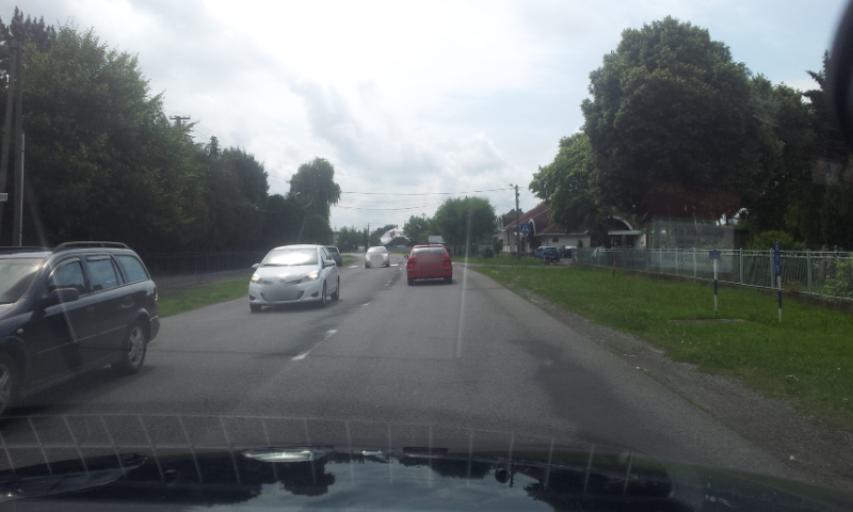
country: SK
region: Kosicky
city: Michalovce
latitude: 48.6943
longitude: 21.9759
